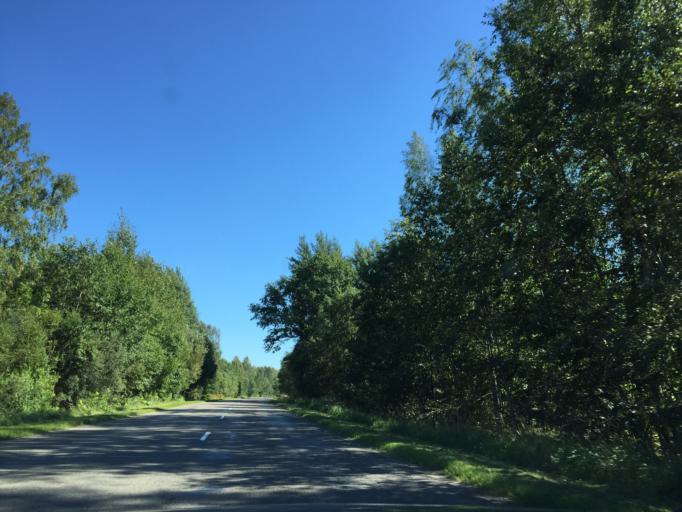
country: LV
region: Akniste
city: Akniste
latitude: 56.1398
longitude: 25.8132
